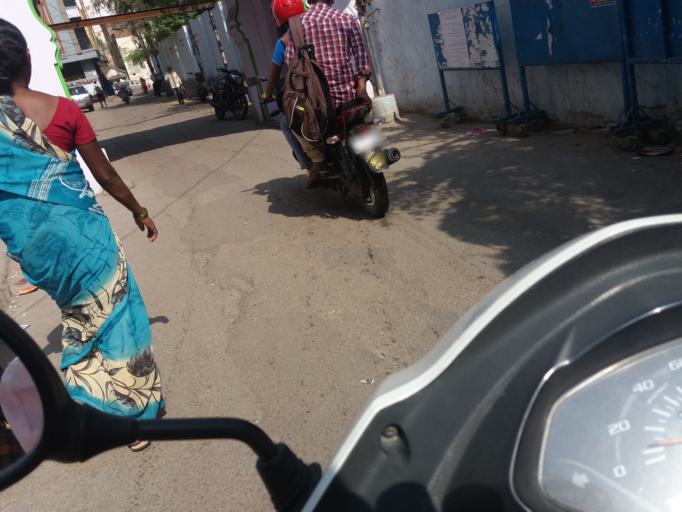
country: IN
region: Telangana
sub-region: Hyderabad
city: Malkajgiri
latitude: 17.4166
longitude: 78.5043
